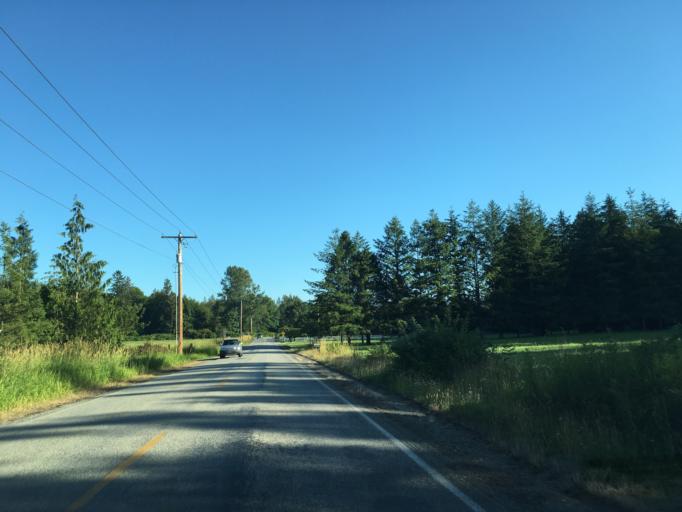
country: US
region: Washington
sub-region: Whatcom County
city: Nooksack
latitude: 48.9373
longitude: -122.2820
